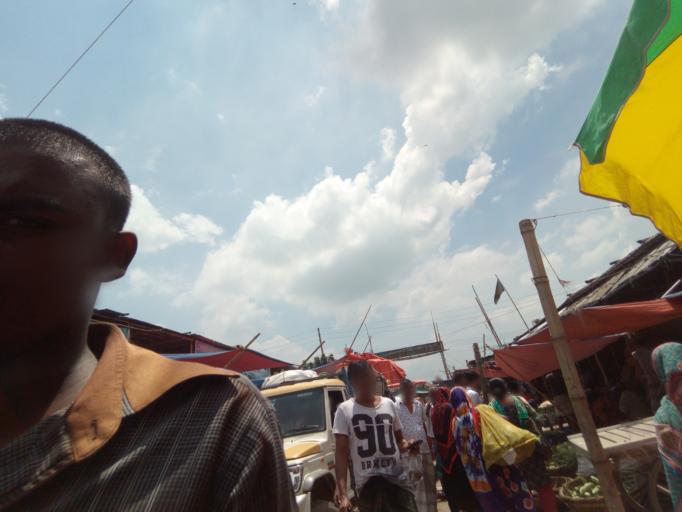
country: BD
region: Dhaka
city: Azimpur
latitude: 23.7474
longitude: 90.3597
